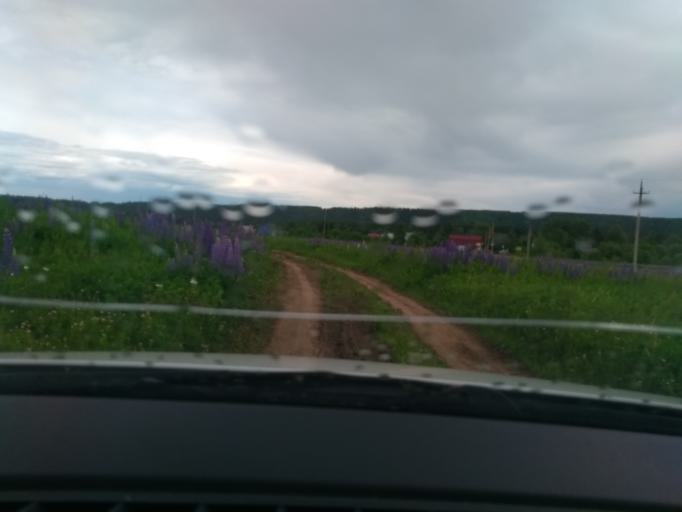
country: RU
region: Perm
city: Sylva
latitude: 57.8412
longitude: 56.7909
